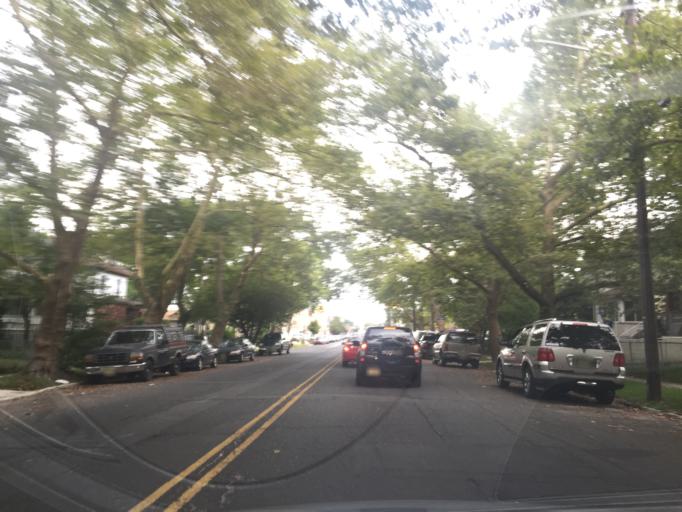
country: US
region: New Jersey
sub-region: Monmouth County
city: Asbury Park
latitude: 40.2216
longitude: -74.0176
